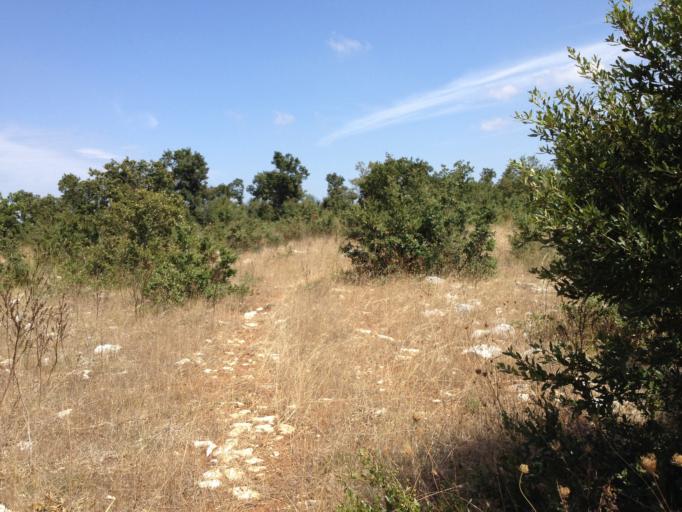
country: IT
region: Apulia
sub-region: Provincia di Bari
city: Gioia del Colle
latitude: 40.8255
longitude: 16.9924
